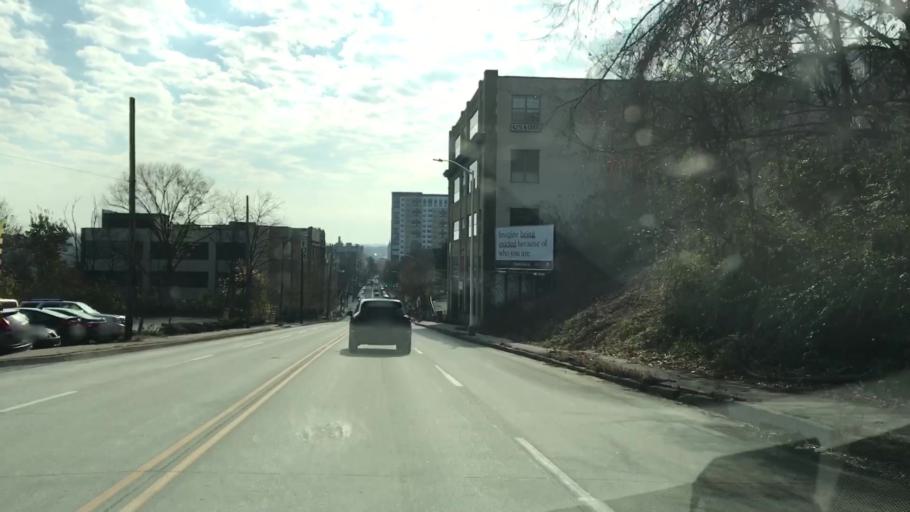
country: US
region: Pennsylvania
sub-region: Allegheny County
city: Bloomfield
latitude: 40.4560
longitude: -79.9546
